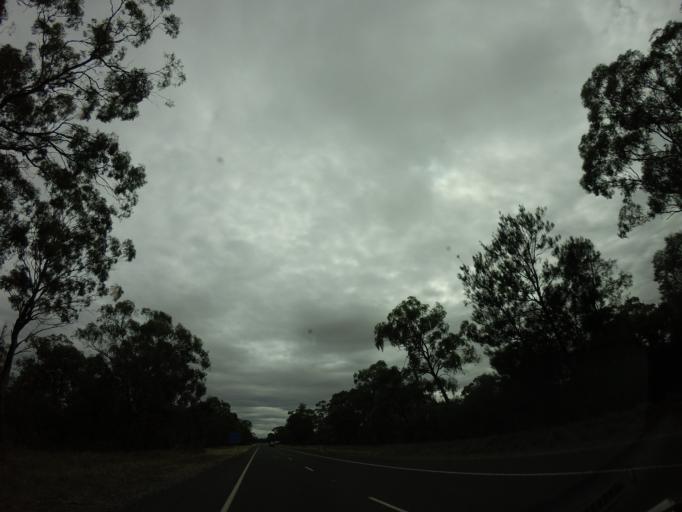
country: AU
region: New South Wales
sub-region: Narrabri
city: Narrabri
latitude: -30.3610
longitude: 149.7399
